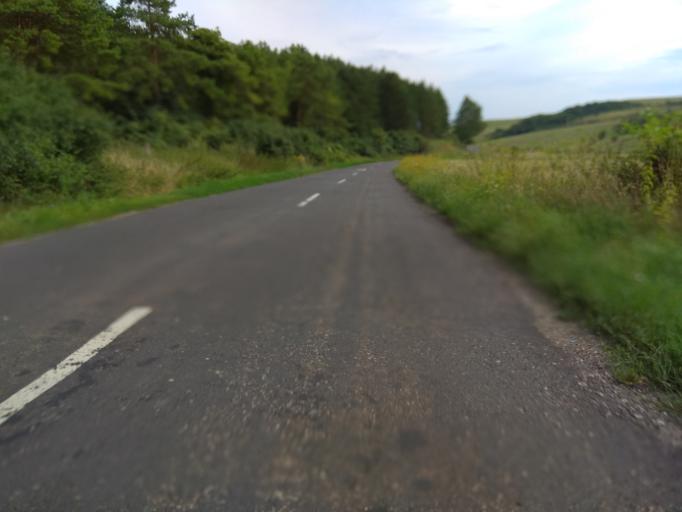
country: HU
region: Heves
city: Tarnalelesz
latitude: 48.0372
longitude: 20.2511
